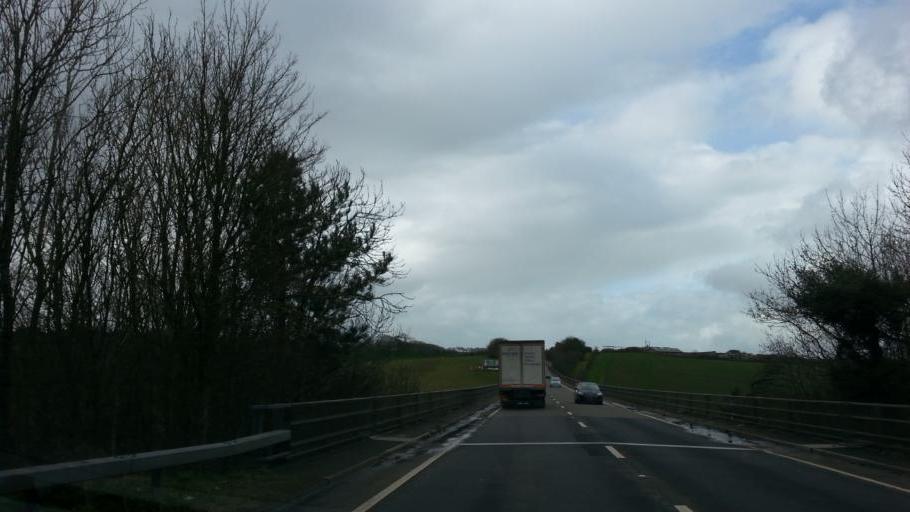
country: GB
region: England
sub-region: Devon
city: Northam
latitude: 51.0242
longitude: -4.2327
